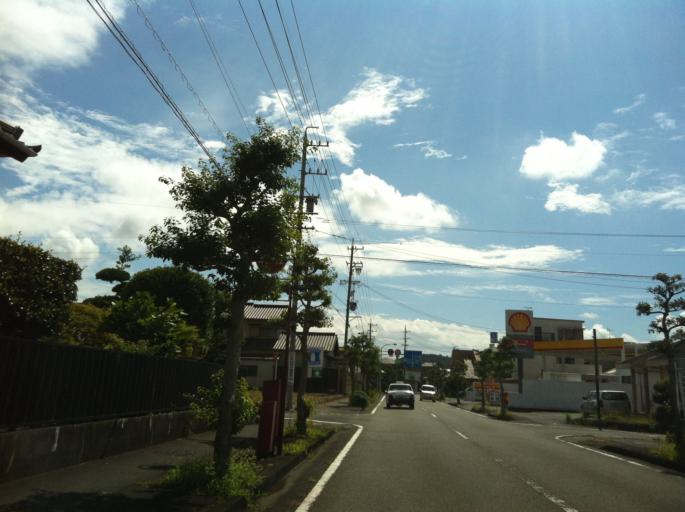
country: JP
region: Shizuoka
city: Kanaya
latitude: 34.8295
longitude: 138.1303
